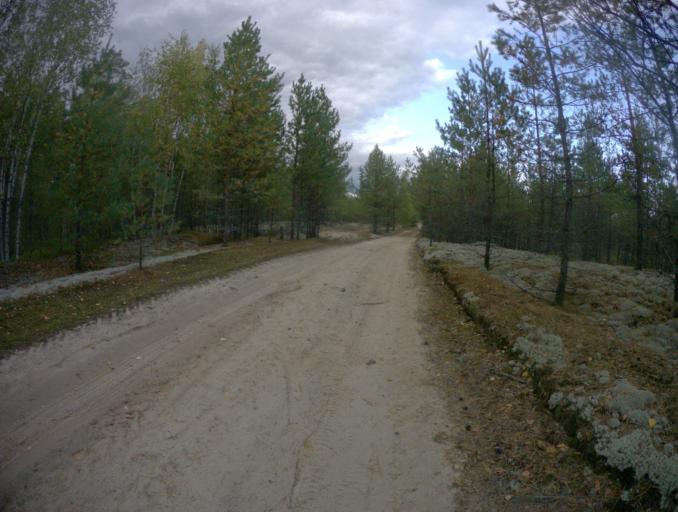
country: RU
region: Vladimir
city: Golovino
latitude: 55.8699
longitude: 40.4001
